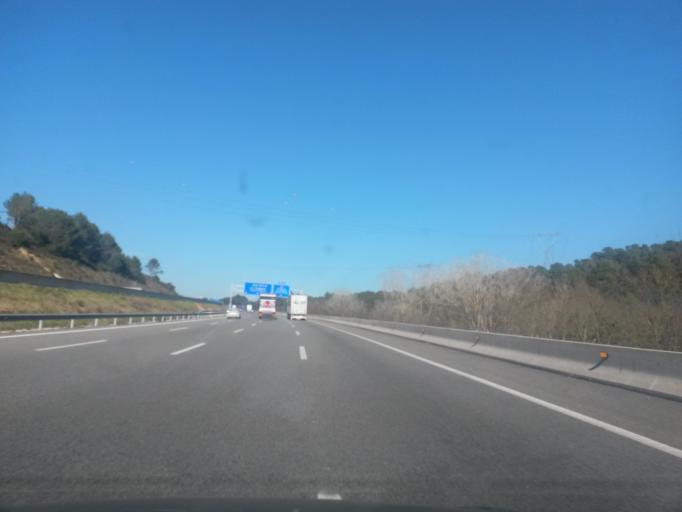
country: ES
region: Catalonia
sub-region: Provincia de Girona
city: Cervia de Ter
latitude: 42.0606
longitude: 2.8850
